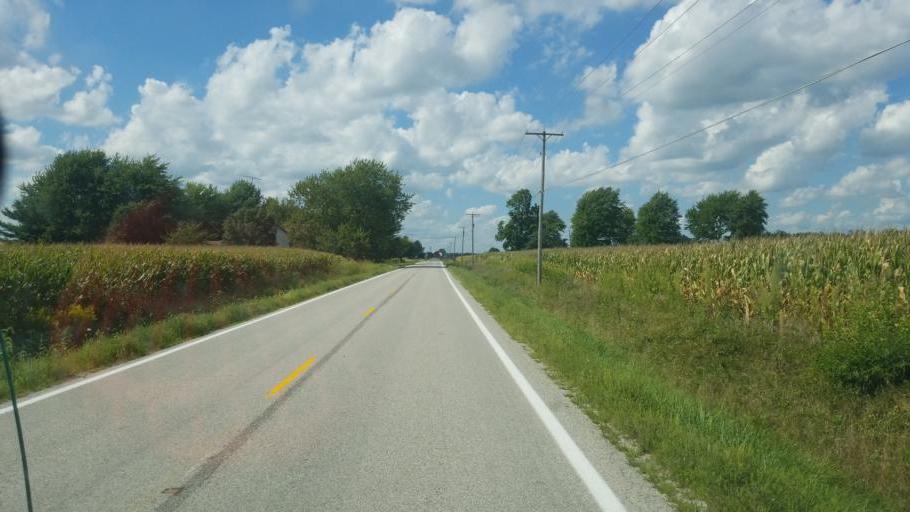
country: US
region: Ohio
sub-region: Union County
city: Richwood
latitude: 40.3739
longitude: -83.2708
